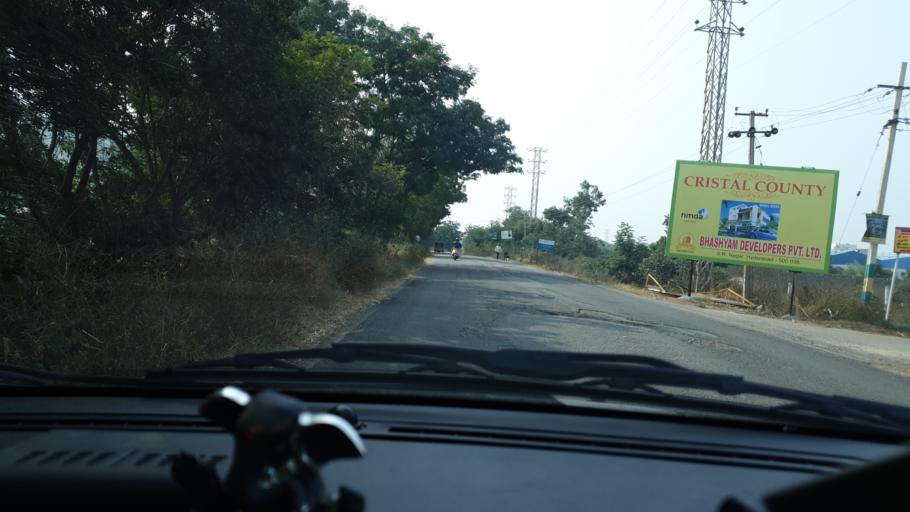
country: IN
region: Telangana
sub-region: Rangareddi
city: Singapur
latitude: 17.4993
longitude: 78.1926
